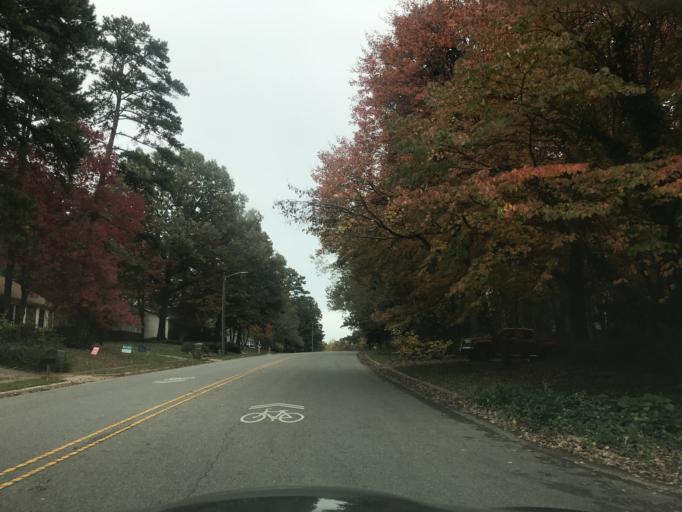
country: US
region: North Carolina
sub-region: Wake County
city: West Raleigh
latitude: 35.8839
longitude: -78.6591
